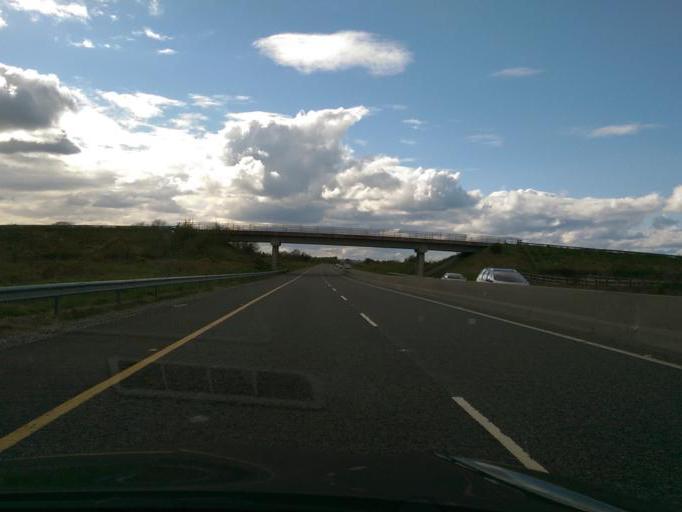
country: IE
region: Leinster
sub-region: An Iarmhi
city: Kilbeggan
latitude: 53.3726
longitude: -7.5437
